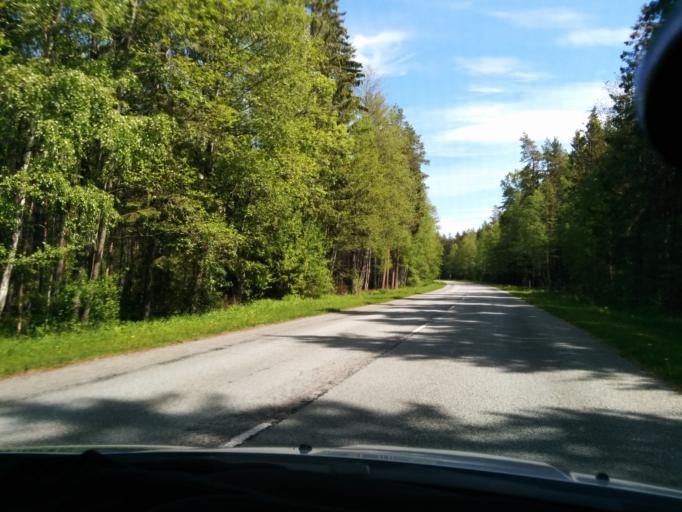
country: EE
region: Harju
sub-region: Loksa linn
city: Loksa
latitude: 59.5625
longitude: 25.9697
